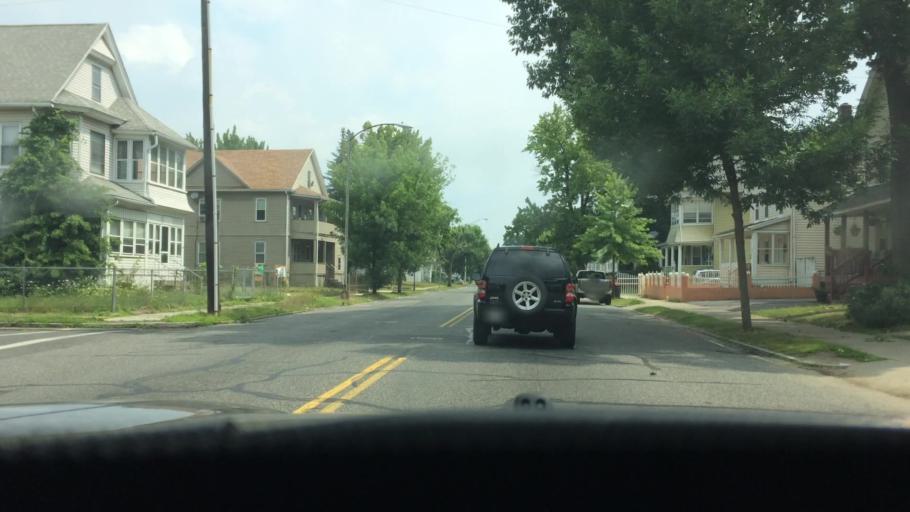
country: US
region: Massachusetts
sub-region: Hampden County
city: Springfield
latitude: 42.1230
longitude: -72.5873
